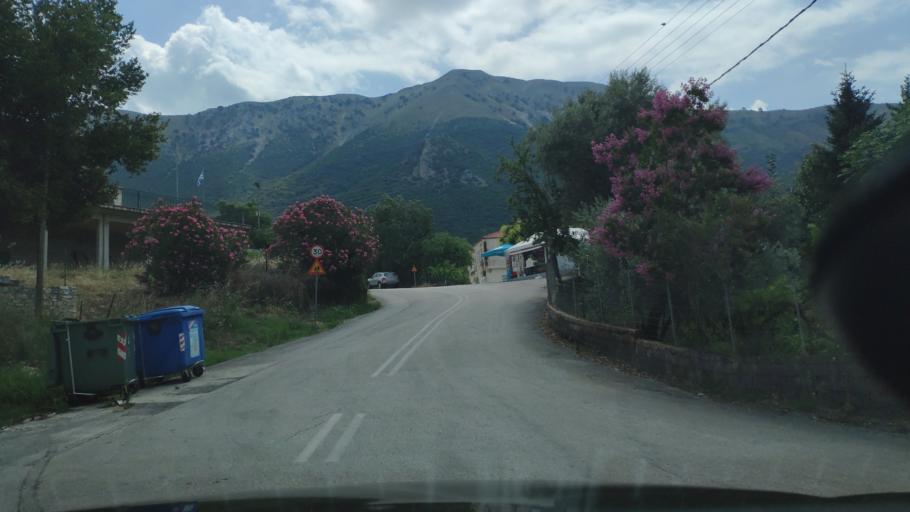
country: GR
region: Epirus
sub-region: Nomos Artas
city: Kampi
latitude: 39.2711
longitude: 20.9409
